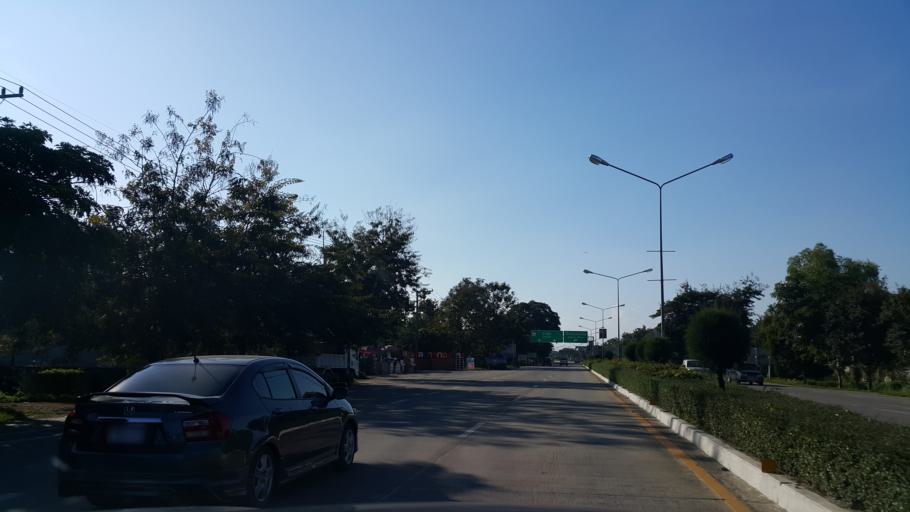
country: TH
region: Lamphun
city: Lamphun
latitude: 18.5702
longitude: 99.0207
